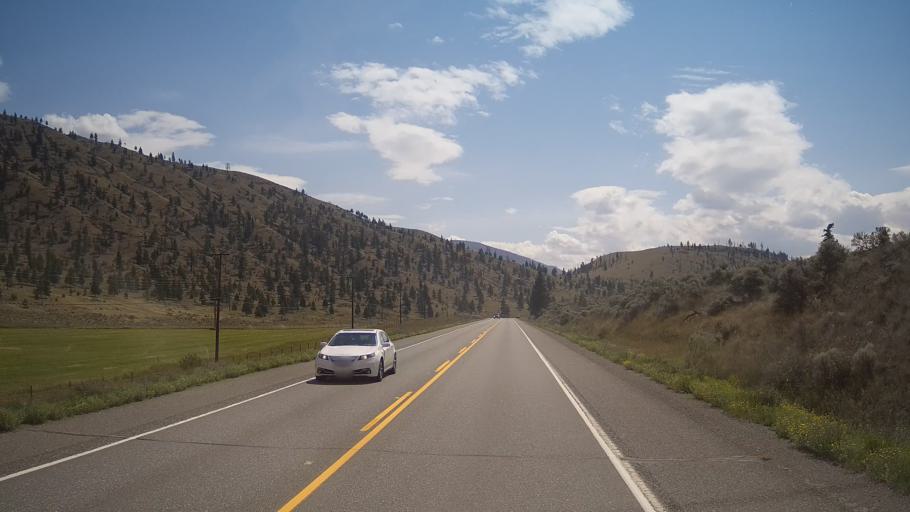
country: CA
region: British Columbia
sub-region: Thompson-Nicola Regional District
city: Ashcroft
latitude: 50.6472
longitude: -121.3504
